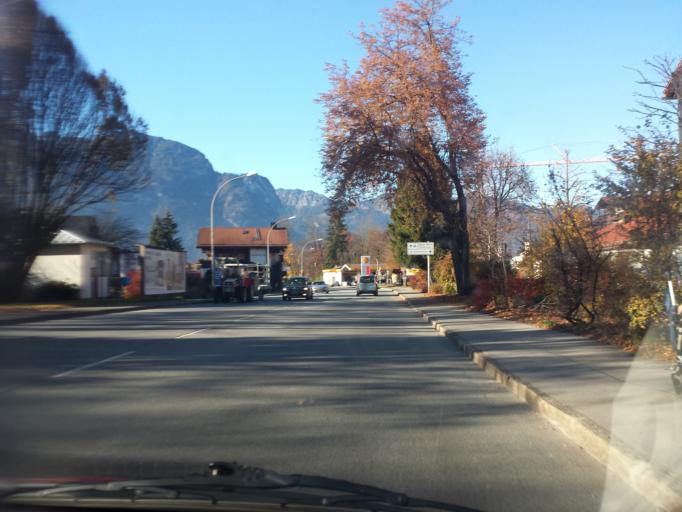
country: DE
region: Bavaria
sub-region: Upper Bavaria
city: Garmisch-Partenkirchen
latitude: 47.4888
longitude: 11.1142
